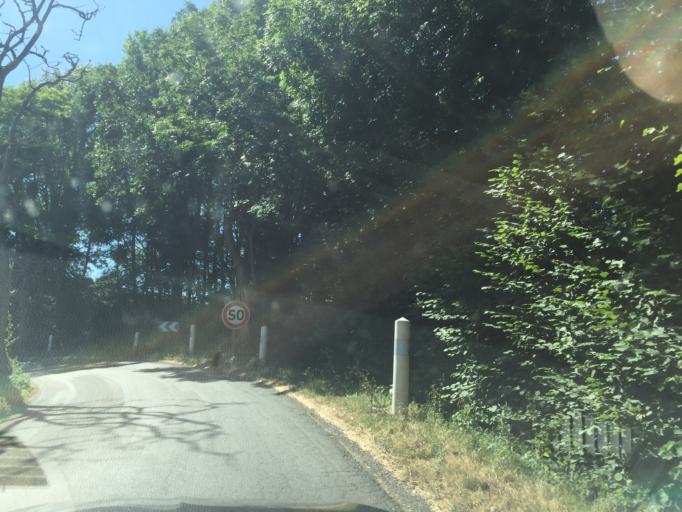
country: FR
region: Poitou-Charentes
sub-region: Departement de la Vienne
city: Vivonne
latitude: 46.4377
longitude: 0.2875
